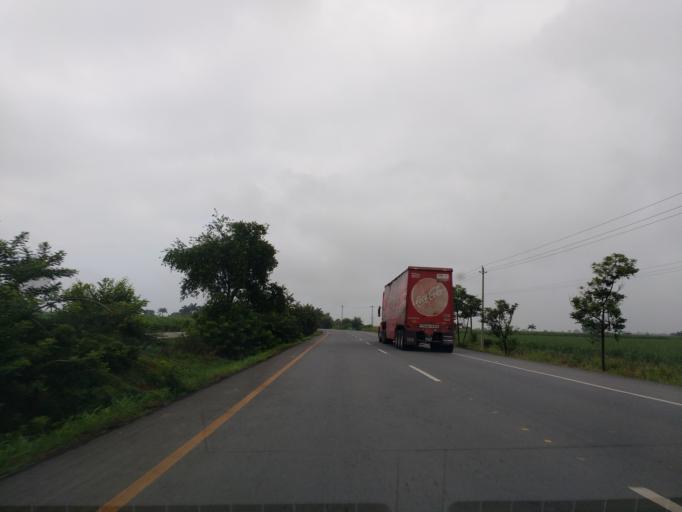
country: CO
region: Valle del Cauca
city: Palmira
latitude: 3.5500
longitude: -76.3382
